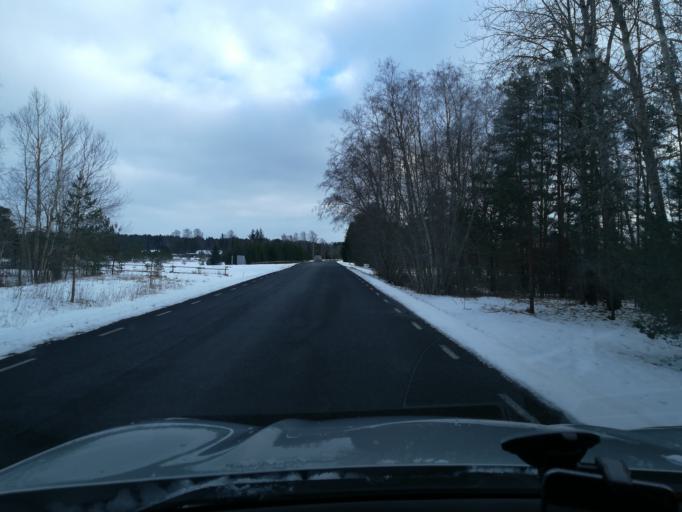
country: EE
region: Harju
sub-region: Keila linn
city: Keila
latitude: 59.4034
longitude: 24.4103
